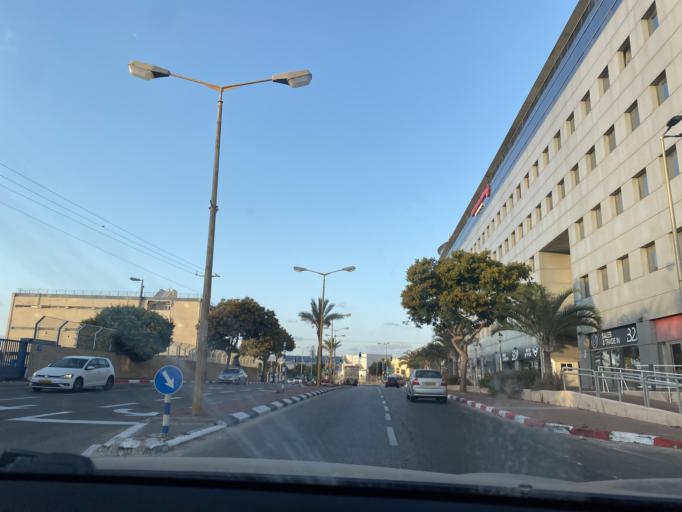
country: IL
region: Southern District
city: Ashdod
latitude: 31.8103
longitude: 34.6596
